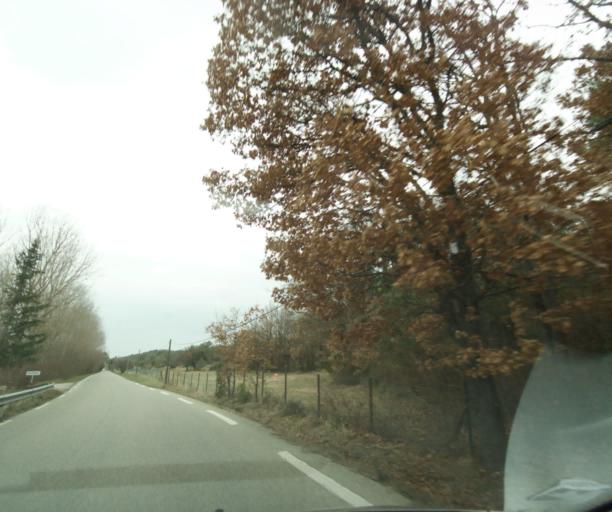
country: FR
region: Provence-Alpes-Cote d'Azur
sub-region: Departement des Bouches-du-Rhone
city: Jouques
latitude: 43.6290
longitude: 5.6618
